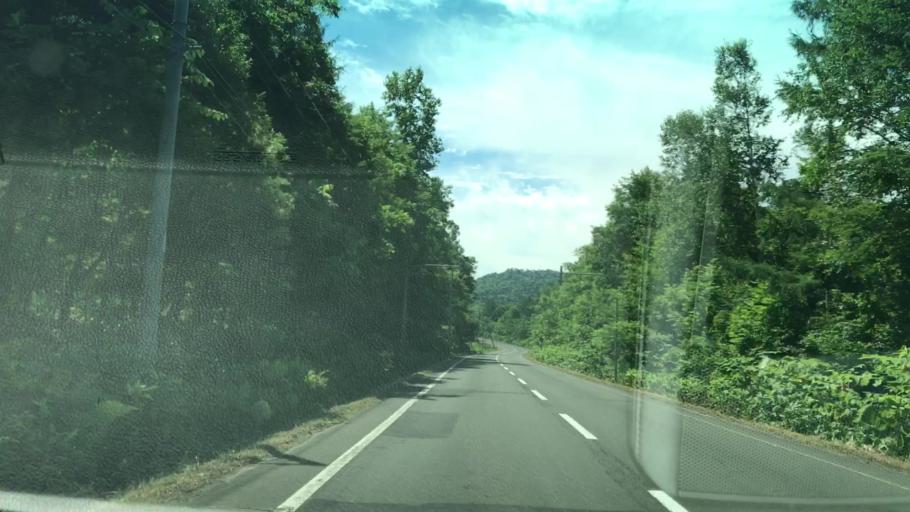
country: JP
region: Hokkaido
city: Shimo-furano
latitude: 42.9617
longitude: 142.4282
